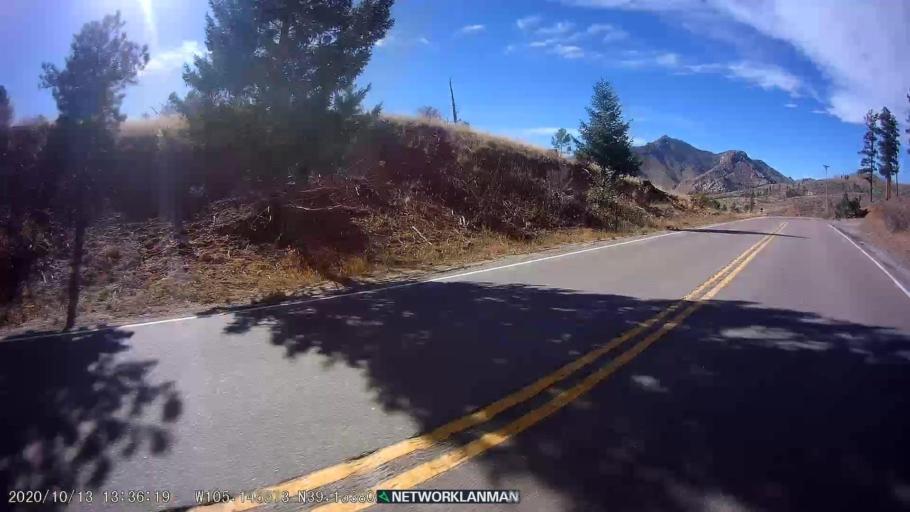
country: US
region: Colorado
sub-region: Teller County
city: Woodland Park
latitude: 39.1545
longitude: -105.1456
